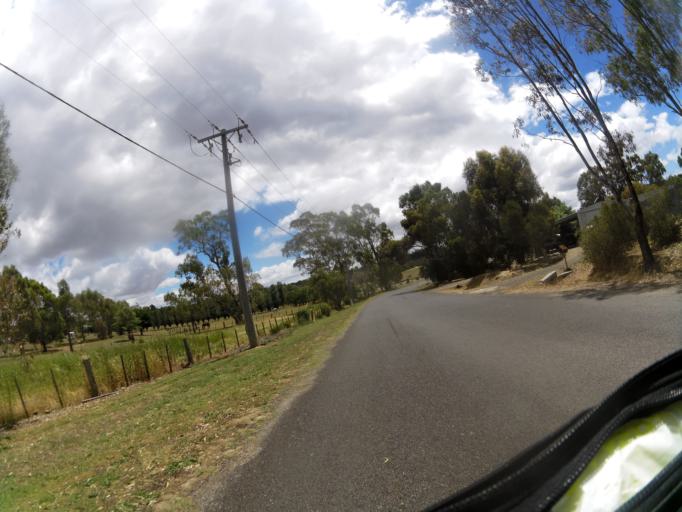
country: AU
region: Victoria
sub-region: Mount Alexander
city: Castlemaine
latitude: -37.0140
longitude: 144.2512
